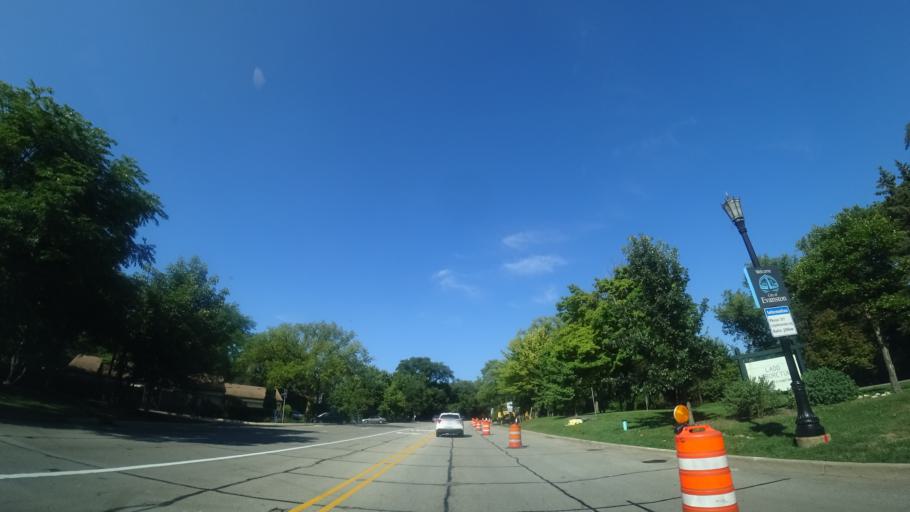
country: US
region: Illinois
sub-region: Cook County
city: Evanston
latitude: 42.0528
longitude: -87.7089
